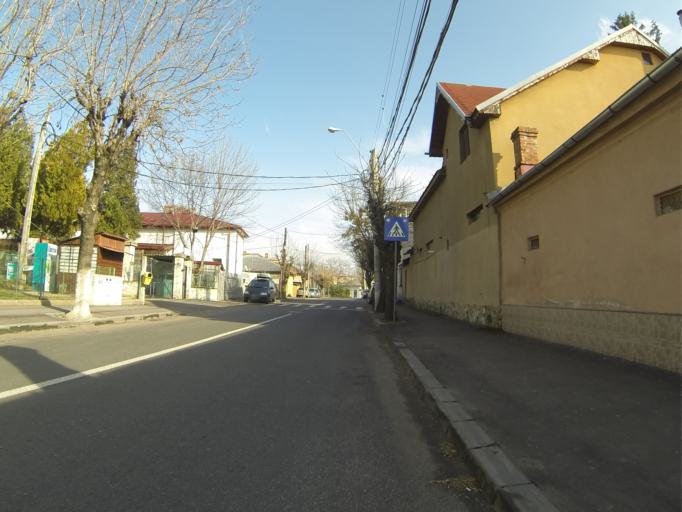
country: RO
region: Dolj
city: Craiova
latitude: 44.3089
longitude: 23.8116
